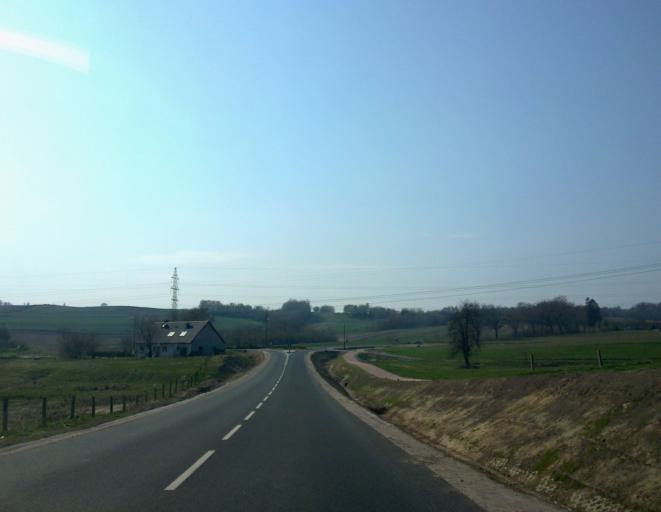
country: PL
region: Pomeranian Voivodeship
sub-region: Powiat wejherowski
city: Gniewino
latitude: 54.6869
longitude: 18.0806
